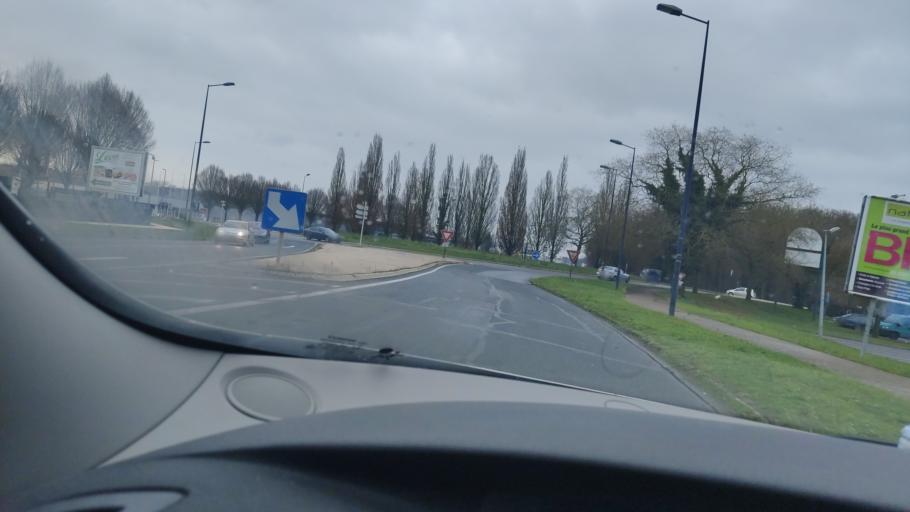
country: FR
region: Ile-de-France
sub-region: Departement de Seine-et-Marne
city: Vert-Saint-Denis
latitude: 48.5661
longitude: 2.6283
